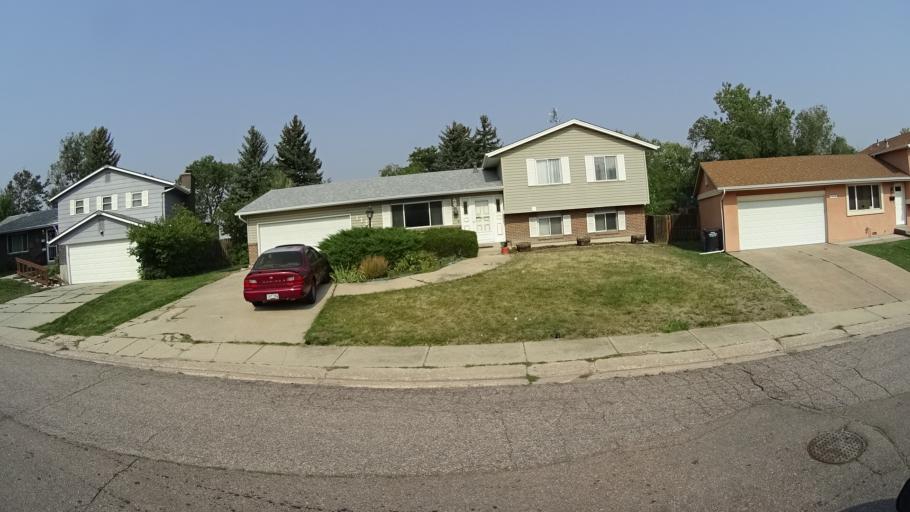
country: US
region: Colorado
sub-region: El Paso County
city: Stratmoor
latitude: 38.8135
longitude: -104.7694
